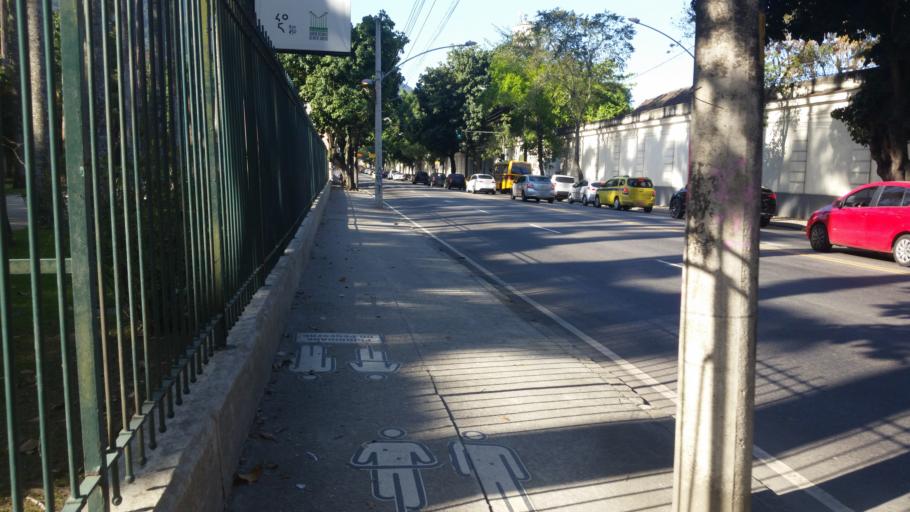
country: BR
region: Rio de Janeiro
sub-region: Rio De Janeiro
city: Rio de Janeiro
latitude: -22.9699
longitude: -43.2223
